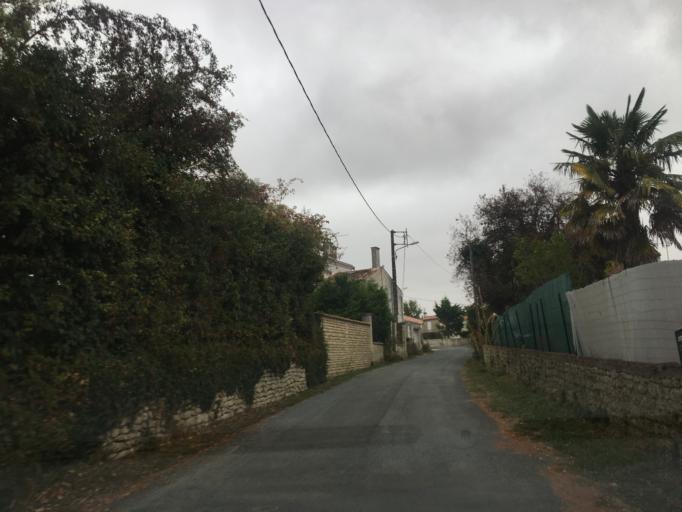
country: FR
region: Poitou-Charentes
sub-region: Departement des Deux-Sevres
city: Beauvoir-sur-Niort
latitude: 46.0771
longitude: -0.4960
